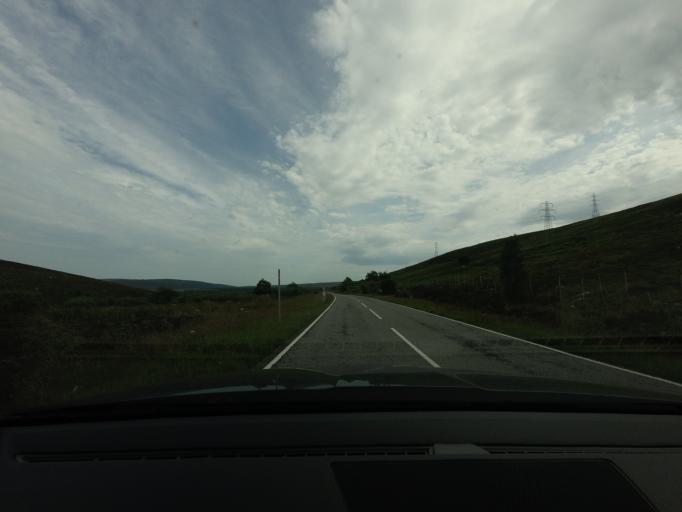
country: GB
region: Scotland
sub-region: Highland
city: Alness
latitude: 57.8260
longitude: -4.2654
